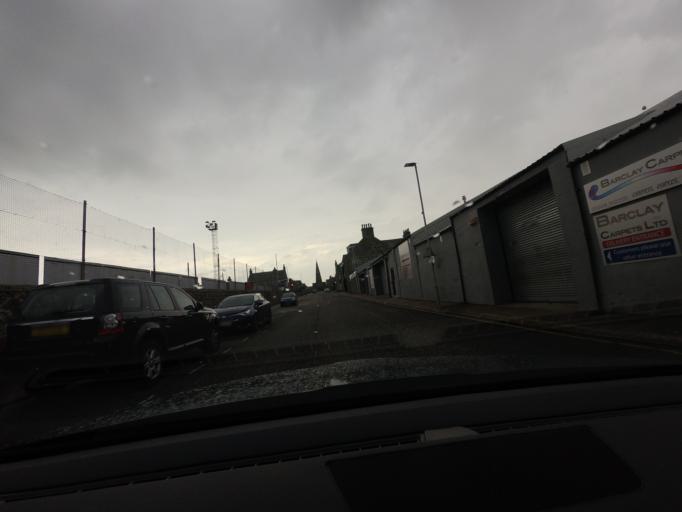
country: GB
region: Scotland
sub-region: Aberdeenshire
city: Fraserburgh
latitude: 57.6900
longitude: -2.0051
